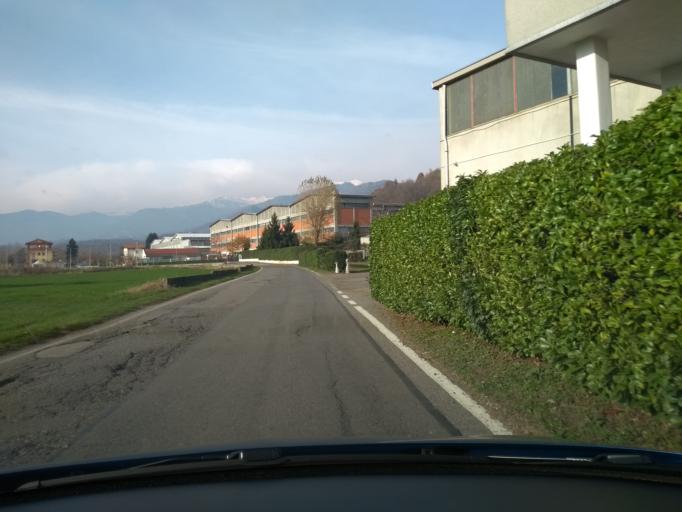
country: IT
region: Piedmont
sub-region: Provincia di Torino
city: Balangero
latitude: 45.2669
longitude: 7.5312
